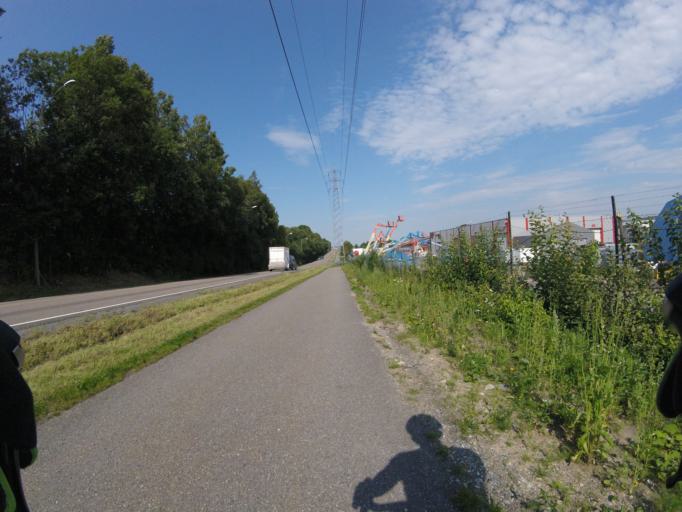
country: NO
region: Akershus
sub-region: Skedsmo
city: Lillestrom
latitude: 59.9687
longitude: 11.0660
